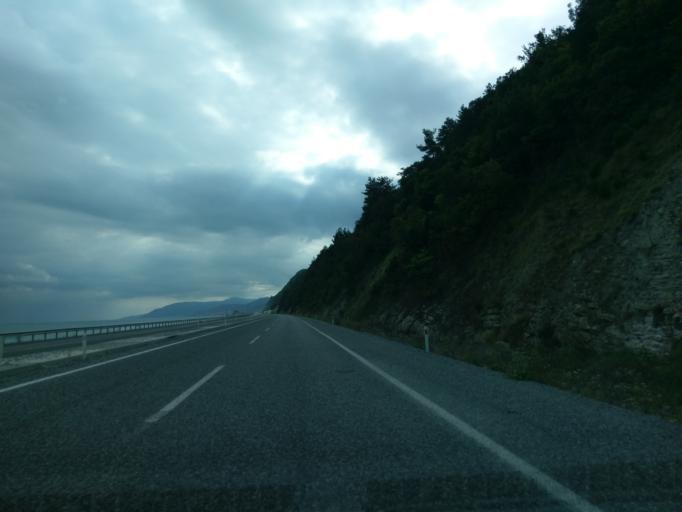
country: TR
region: Kastamonu
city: Catalzeytin
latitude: 41.9487
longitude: 34.2478
